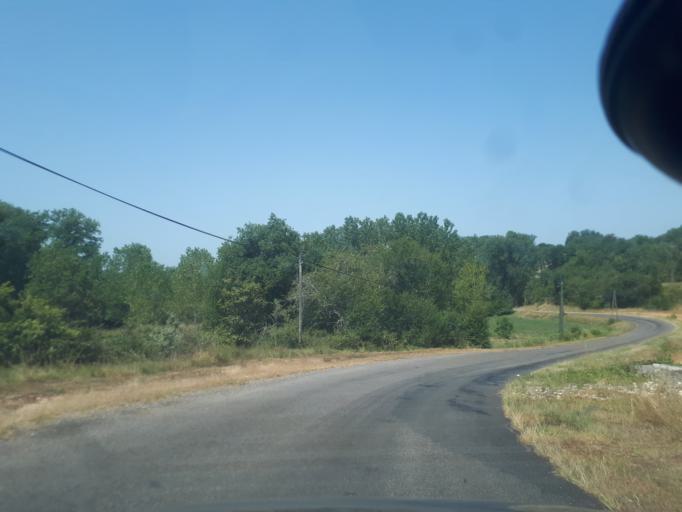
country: FR
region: Midi-Pyrenees
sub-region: Departement du Lot
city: Salviac
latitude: 44.7343
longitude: 1.2819
